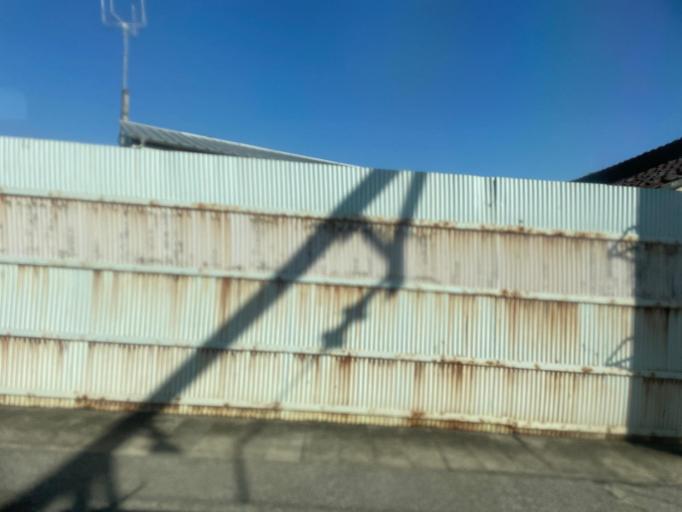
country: JP
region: Yamanashi
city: Ryuo
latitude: 35.5607
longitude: 138.5017
